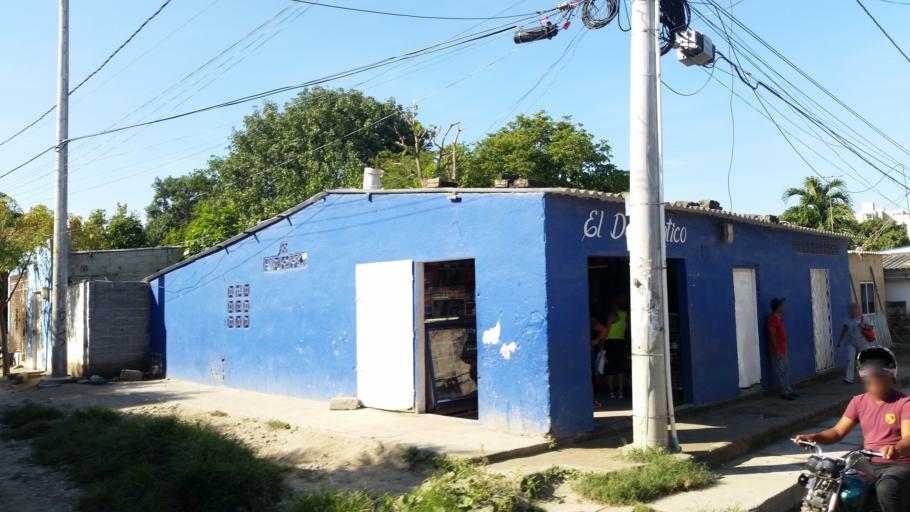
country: CO
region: Magdalena
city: Santa Marta
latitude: 11.1492
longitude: -74.2187
